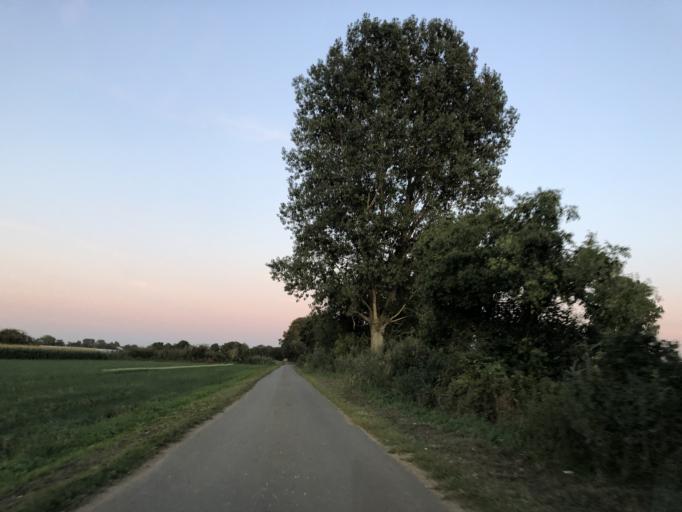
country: DE
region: Hesse
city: Griesheim
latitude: 49.8431
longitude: 8.5402
